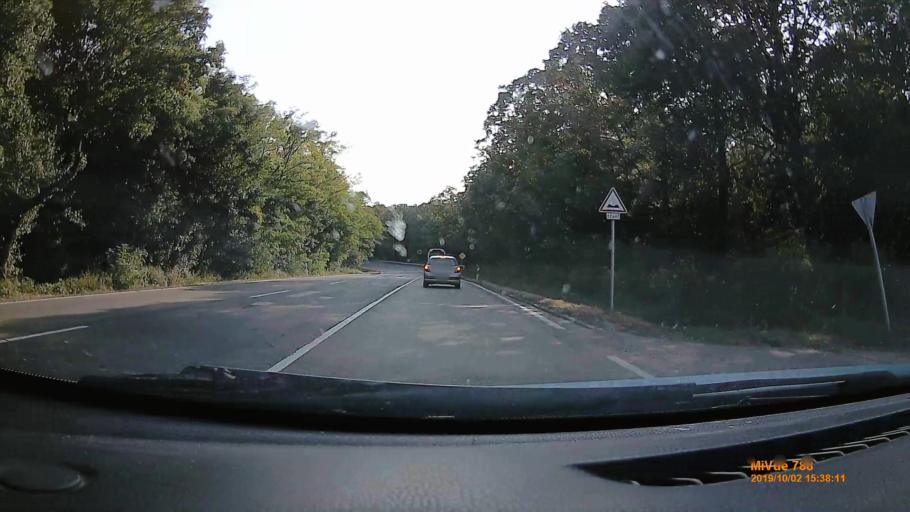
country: HU
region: Heves
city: Kerecsend
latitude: 47.8311
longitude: 20.3566
